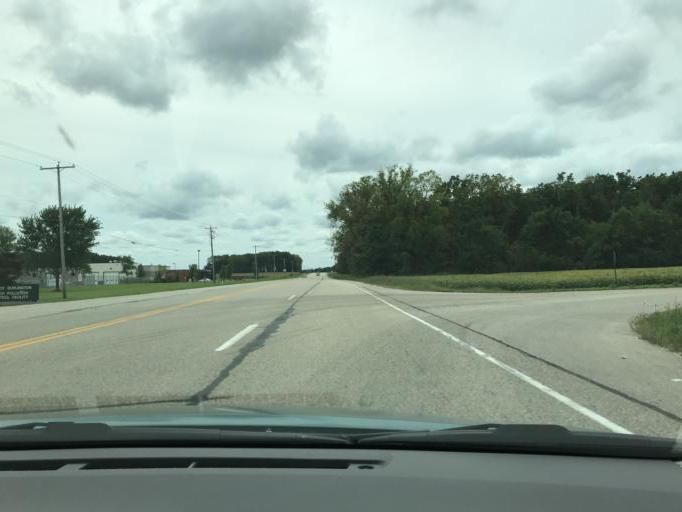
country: US
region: Wisconsin
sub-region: Racine County
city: Burlington
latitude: 42.6502
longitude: -88.2558
